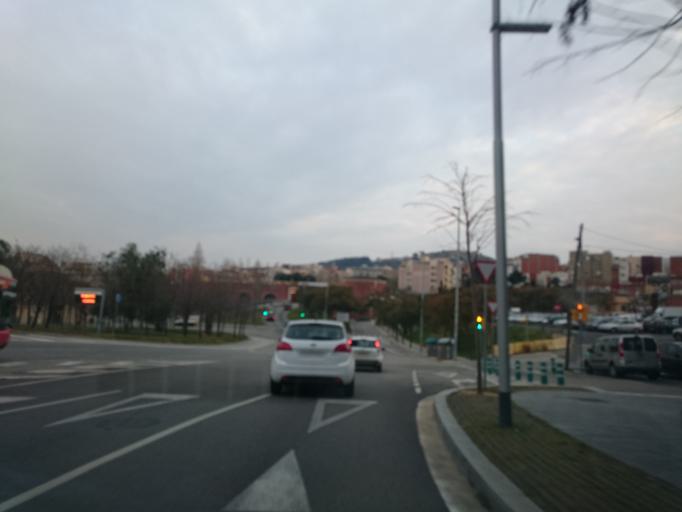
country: ES
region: Catalonia
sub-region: Provincia de Barcelona
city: Horta-Guinardo
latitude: 41.4304
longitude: 2.1555
